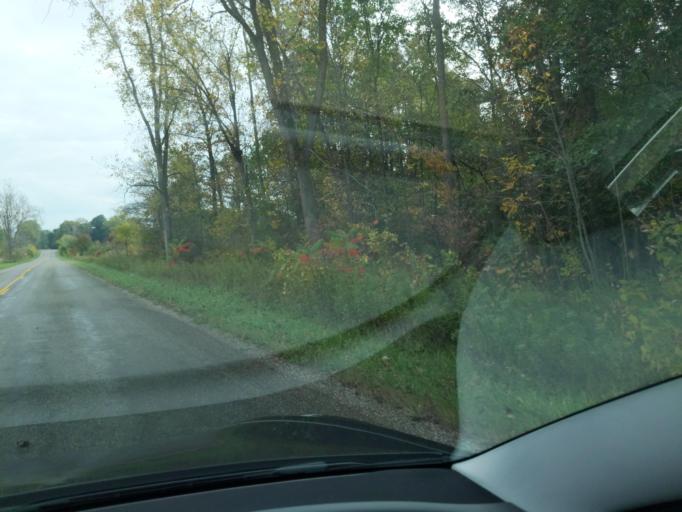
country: US
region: Michigan
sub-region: Eaton County
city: Eaton Rapids
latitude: 42.4763
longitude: -84.6290
